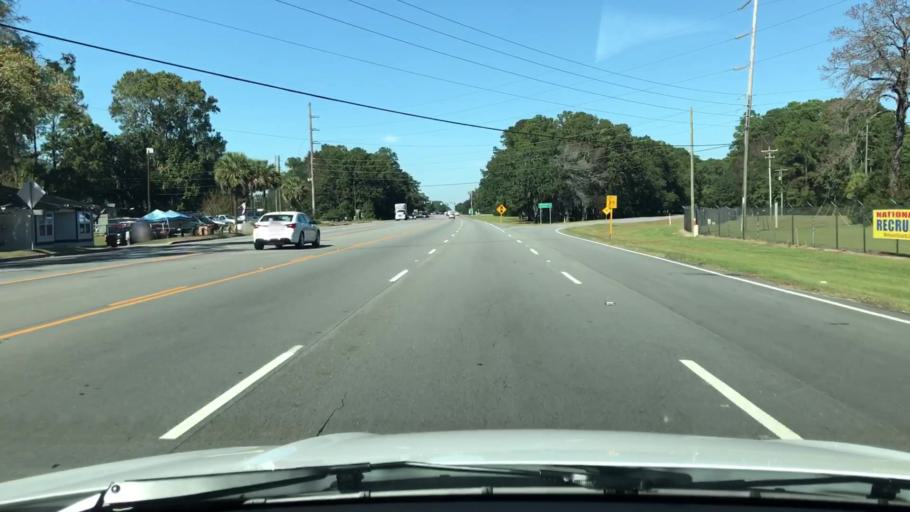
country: US
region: South Carolina
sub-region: Beaufort County
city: Burton
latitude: 32.4541
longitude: -80.7326
